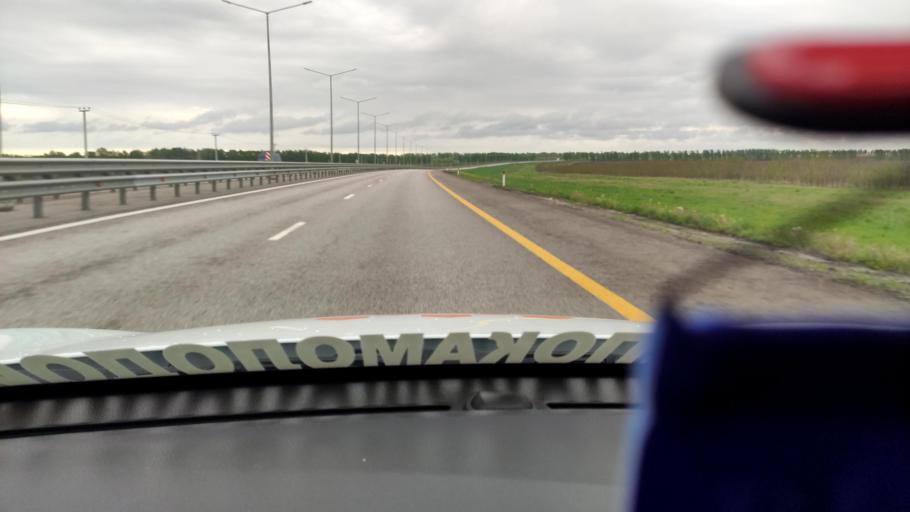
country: RU
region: Voronezj
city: Podkletnoye
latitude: 51.5864
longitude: 39.4487
